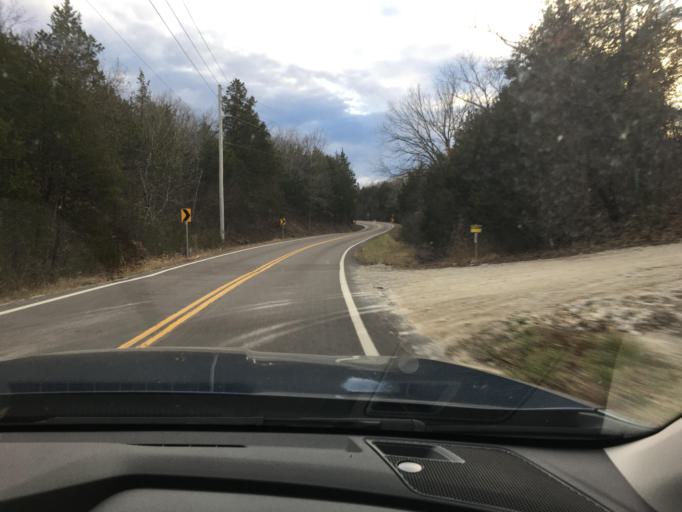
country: US
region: Missouri
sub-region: Jefferson County
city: De Soto
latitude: 38.1048
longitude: -90.5599
